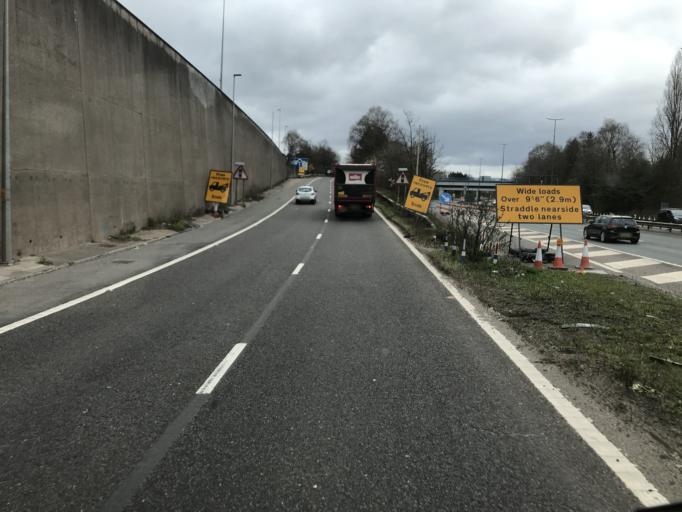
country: GB
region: England
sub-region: City and Borough of Salford
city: Eccles
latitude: 53.4862
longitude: -2.3346
